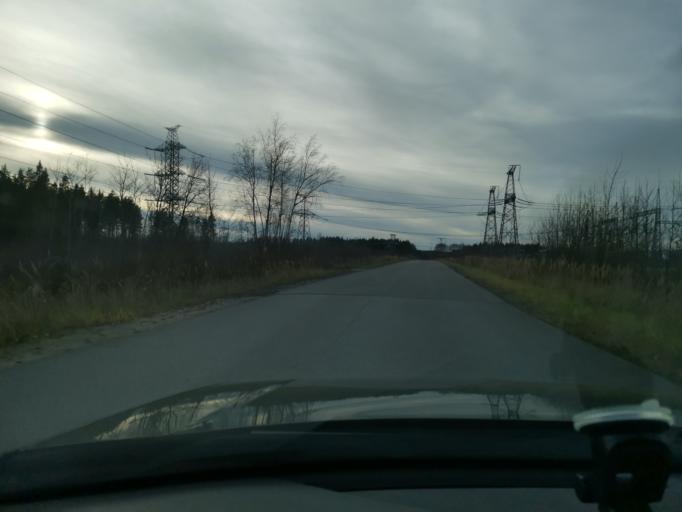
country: EE
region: Ida-Virumaa
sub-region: Sillamaee linn
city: Sillamae
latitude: 59.2691
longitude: 27.9126
